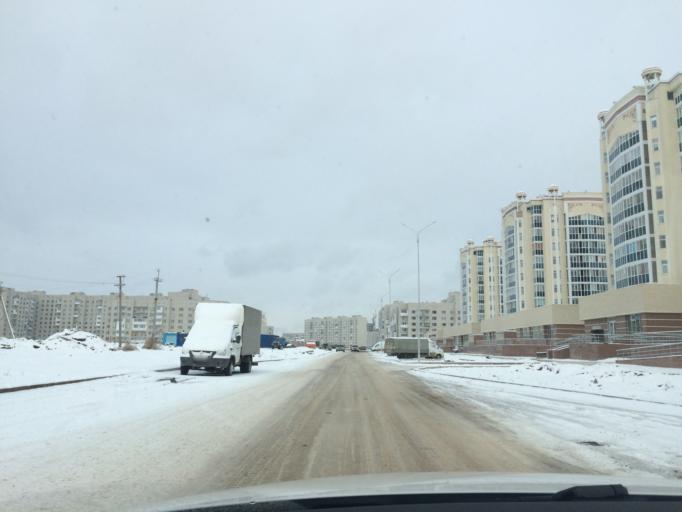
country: KZ
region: Astana Qalasy
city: Astana
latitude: 51.1201
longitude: 71.5035
